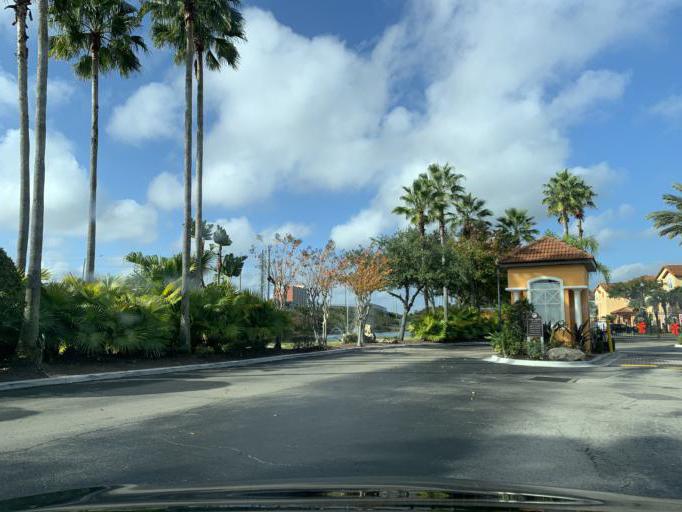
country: US
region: Florida
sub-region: Orange County
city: Tangelo Park
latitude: 28.4833
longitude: -81.4500
